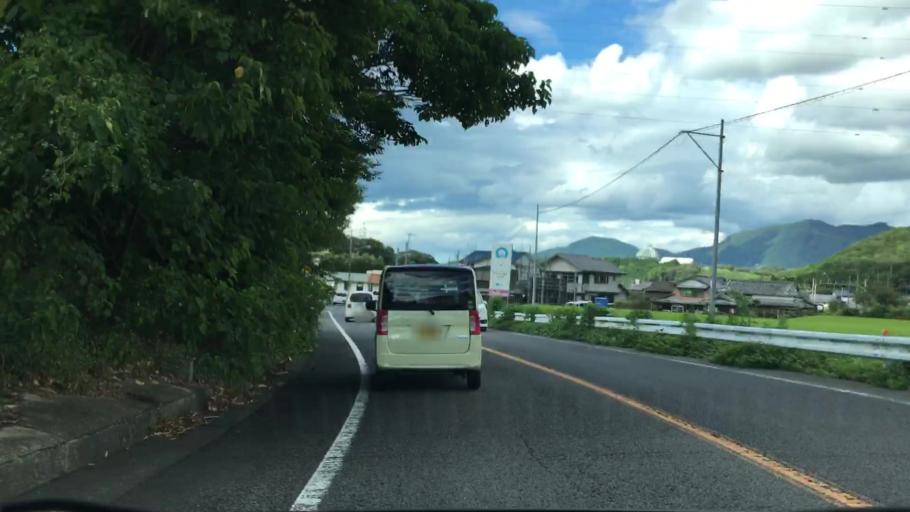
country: JP
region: Saga Prefecture
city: Imaricho-ko
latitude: 33.1776
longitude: 129.8520
